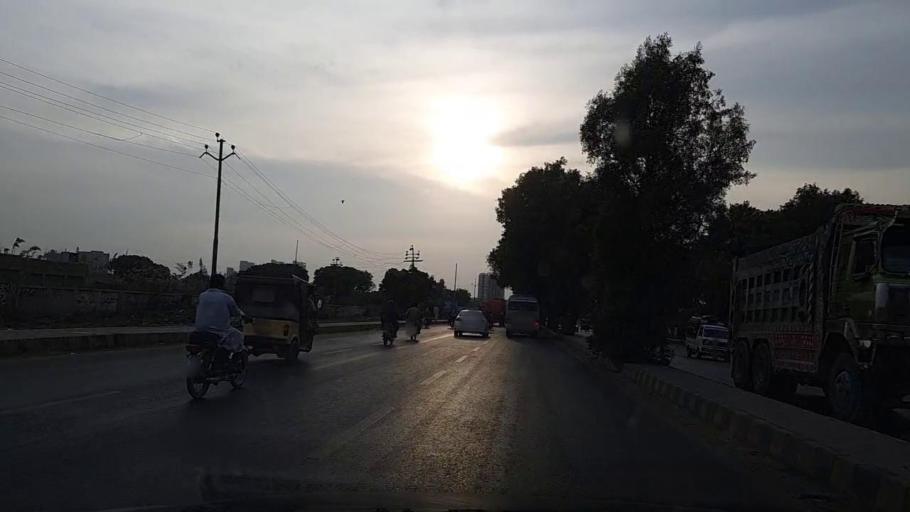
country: PK
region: Sindh
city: Malir Cantonment
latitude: 24.8544
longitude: 67.2524
